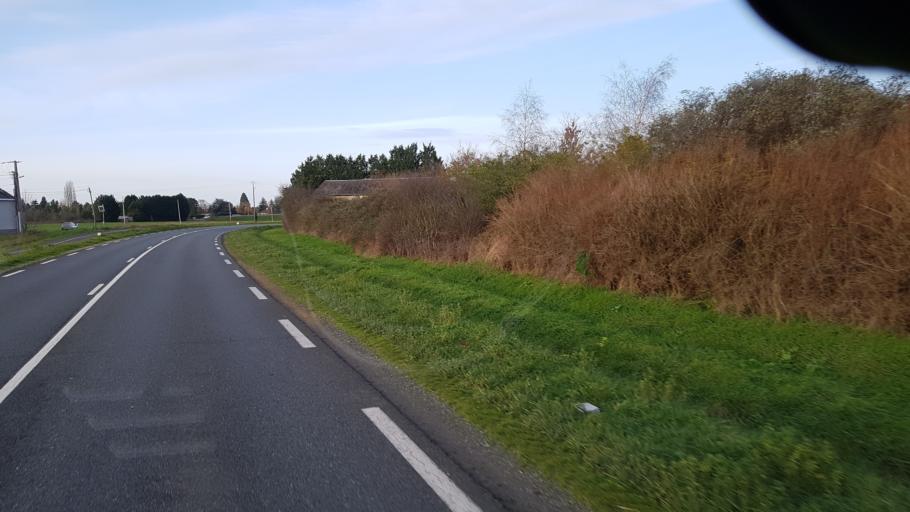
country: FR
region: Centre
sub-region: Departement de l'Indre
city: Chateauroux
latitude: 46.7866
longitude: 1.6824
